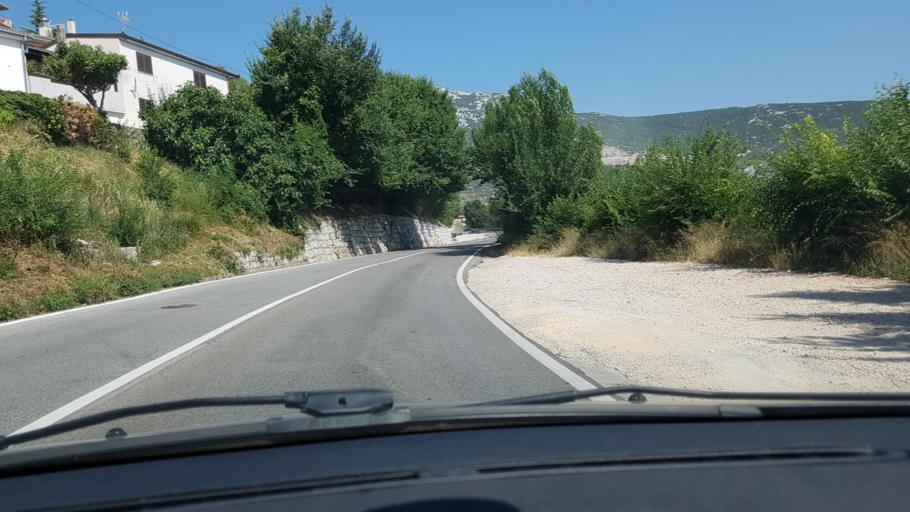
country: HR
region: Splitsko-Dalmatinska
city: Klis
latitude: 43.5585
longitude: 16.5203
